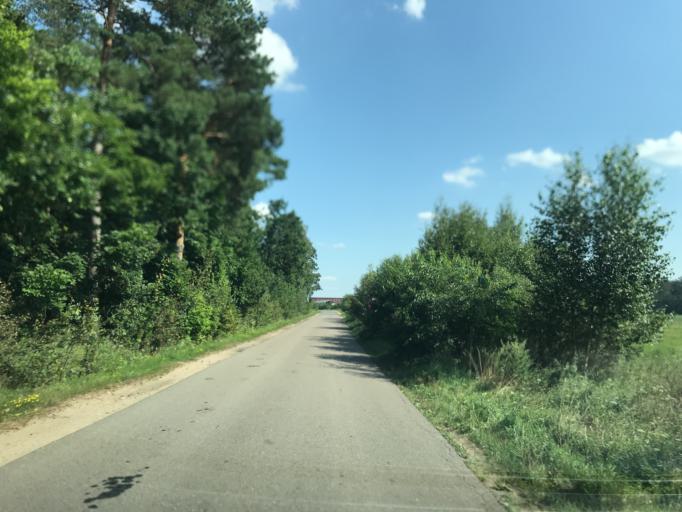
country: PL
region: Masovian Voivodeship
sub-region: Powiat zurominski
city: Lubowidz
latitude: 53.1575
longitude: 19.9125
